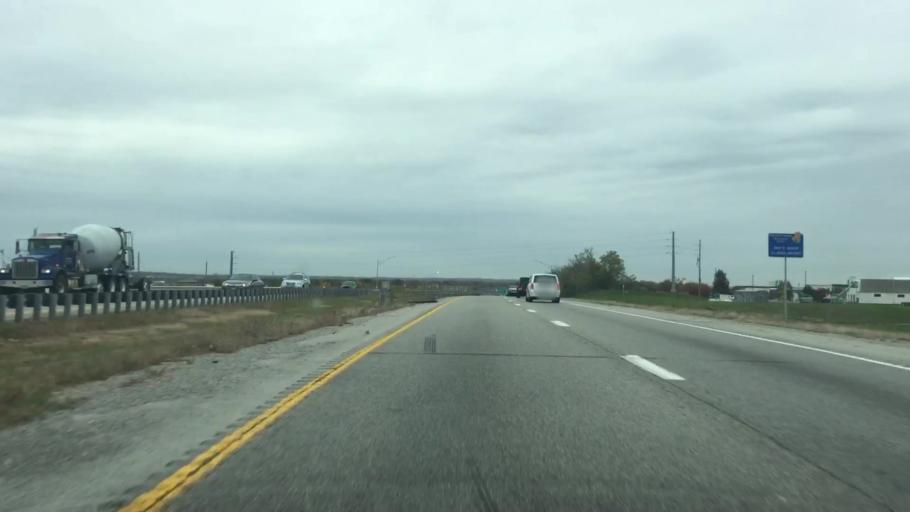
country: US
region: Missouri
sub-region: Jackson County
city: Lees Summit
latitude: 38.9263
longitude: -94.4043
